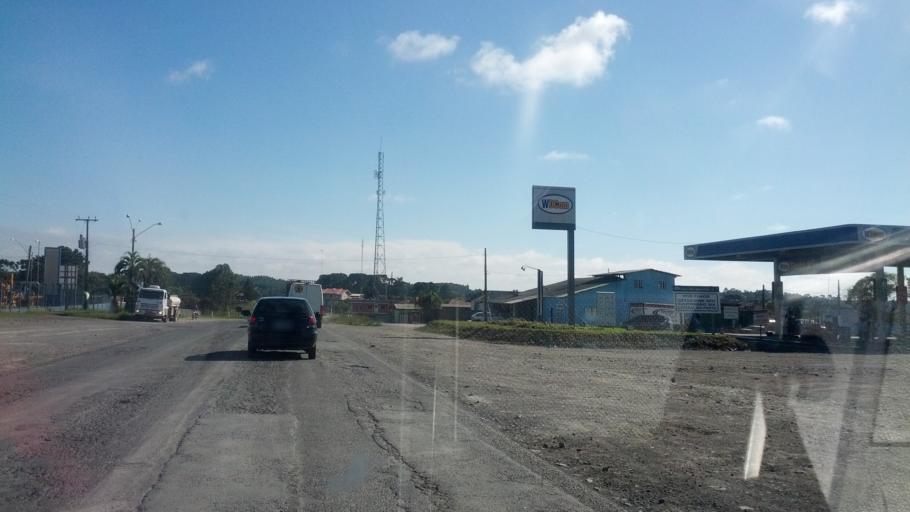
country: BR
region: Santa Catarina
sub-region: Otacilio Costa
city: Otacilio Costa
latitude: -27.5820
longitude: -50.1627
